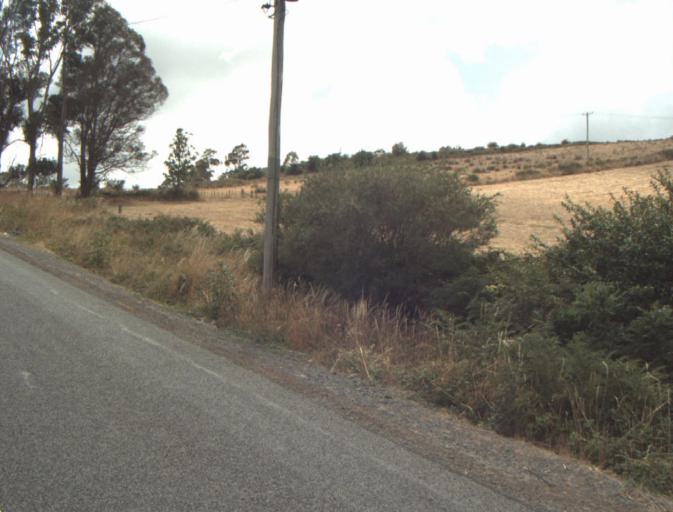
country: AU
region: Tasmania
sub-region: Dorset
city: Bridport
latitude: -41.1703
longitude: 147.2304
